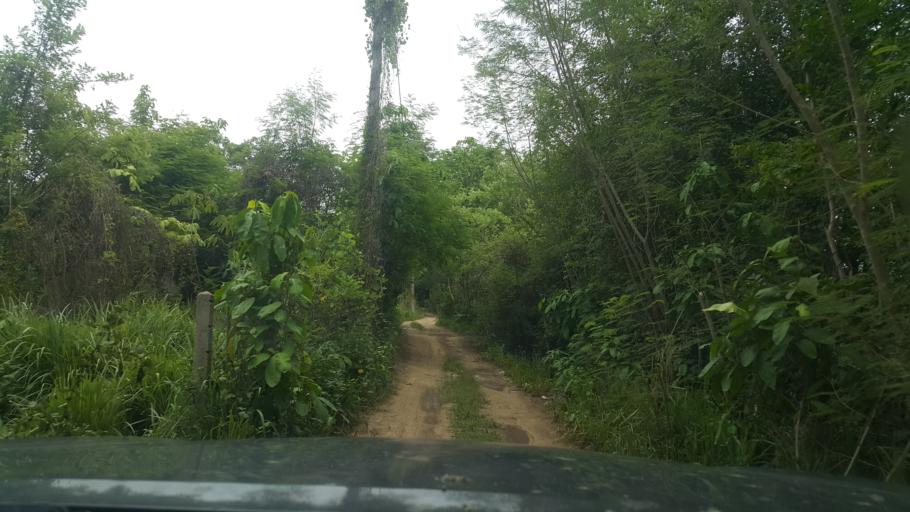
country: TH
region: Chiang Mai
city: Hang Dong
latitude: 18.6812
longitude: 98.8928
